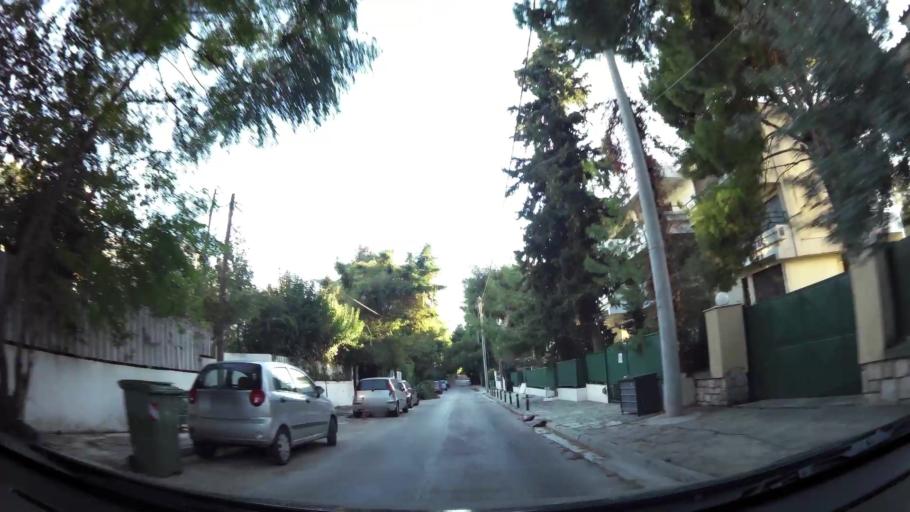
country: GR
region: Attica
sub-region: Nomarchia Athinas
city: Nea Erythraia
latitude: 38.0922
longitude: 23.8256
